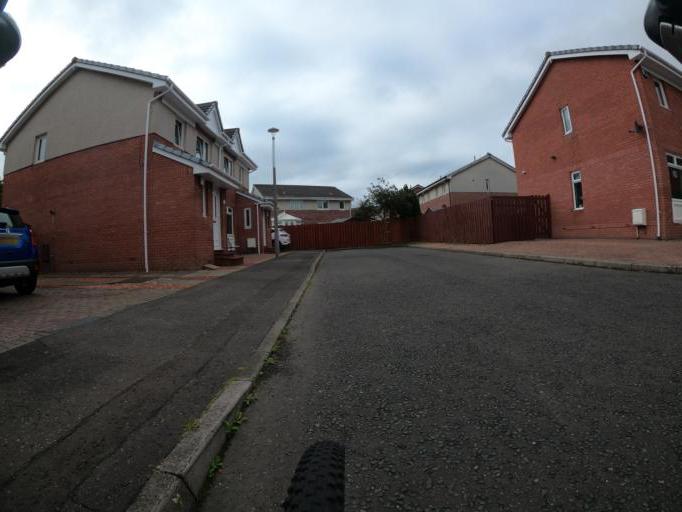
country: GB
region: Scotland
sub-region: Edinburgh
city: Edinburgh
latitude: 55.9742
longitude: -3.2481
